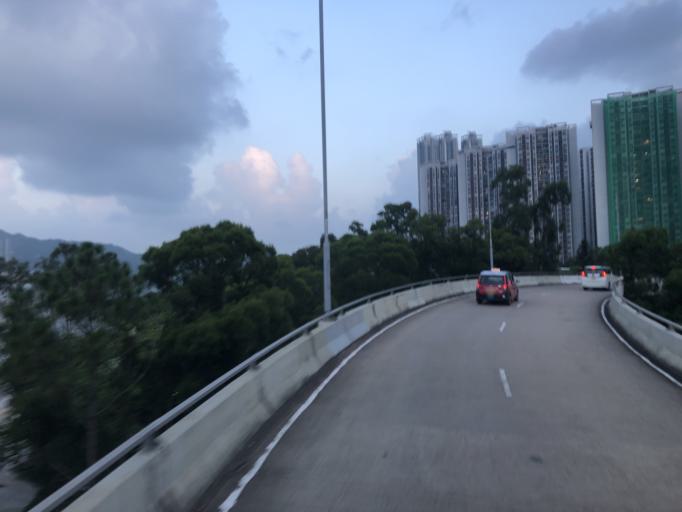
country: HK
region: Kowloon City
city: Kowloon
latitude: 22.2895
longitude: 114.2172
